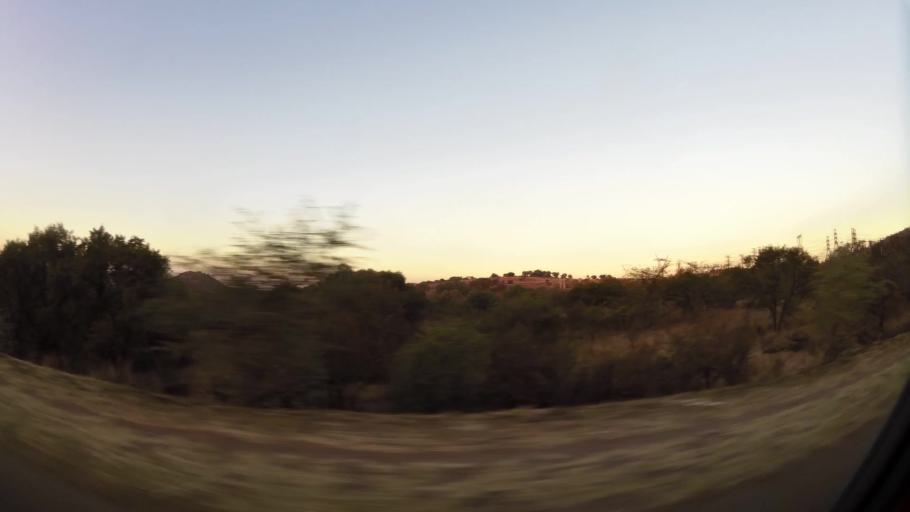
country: ZA
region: North-West
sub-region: Bojanala Platinum District Municipality
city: Rustenburg
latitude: -25.6283
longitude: 27.1866
